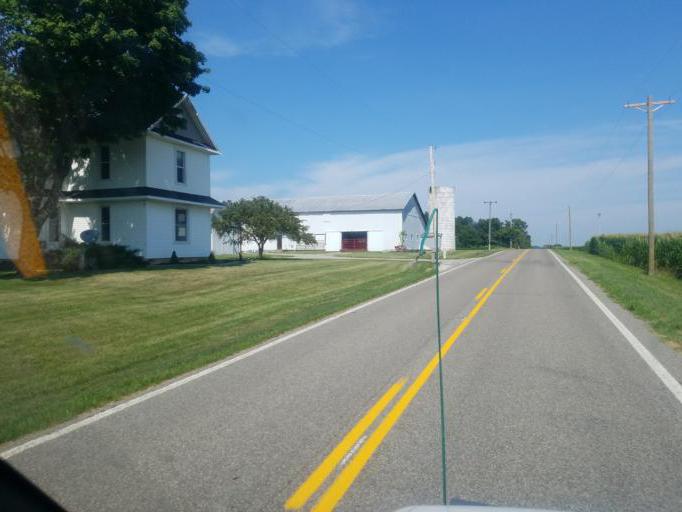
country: US
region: Ohio
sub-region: Shelby County
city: Jackson Center
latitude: 40.4976
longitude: -84.0424
